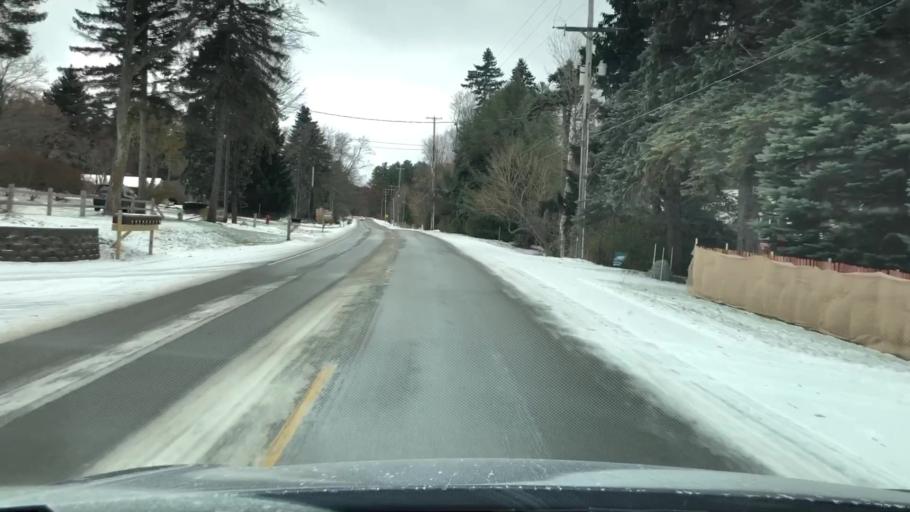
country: US
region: Michigan
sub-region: Grand Traverse County
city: Traverse City
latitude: 44.7783
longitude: -85.5907
